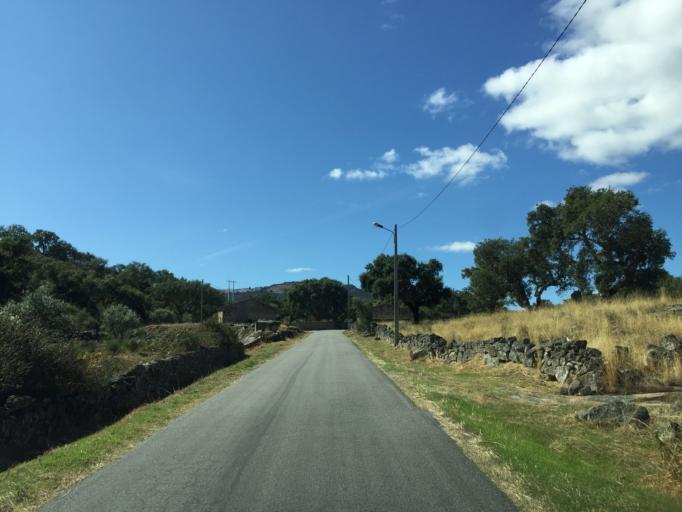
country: PT
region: Portalegre
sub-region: Marvao
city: Marvao
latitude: 39.4210
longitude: -7.3603
